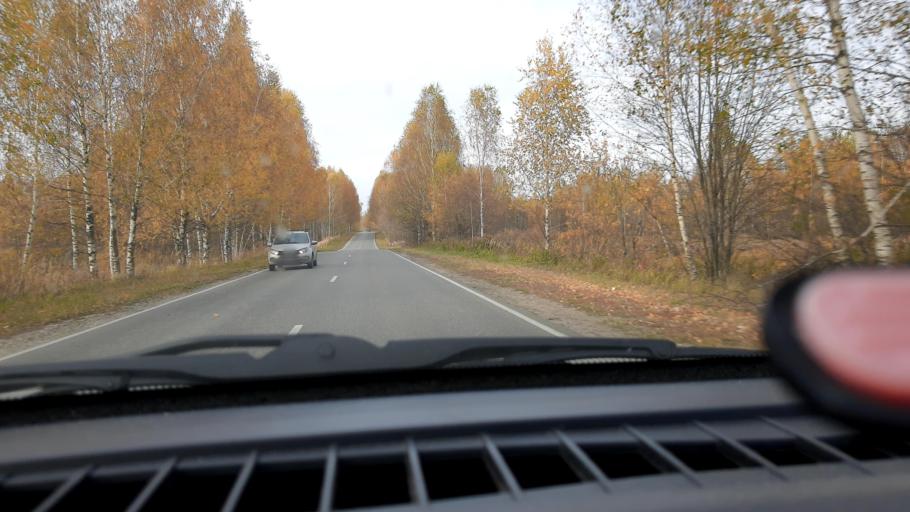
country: RU
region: Nizjnij Novgorod
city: Neklyudovo
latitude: 56.4698
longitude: 43.8895
